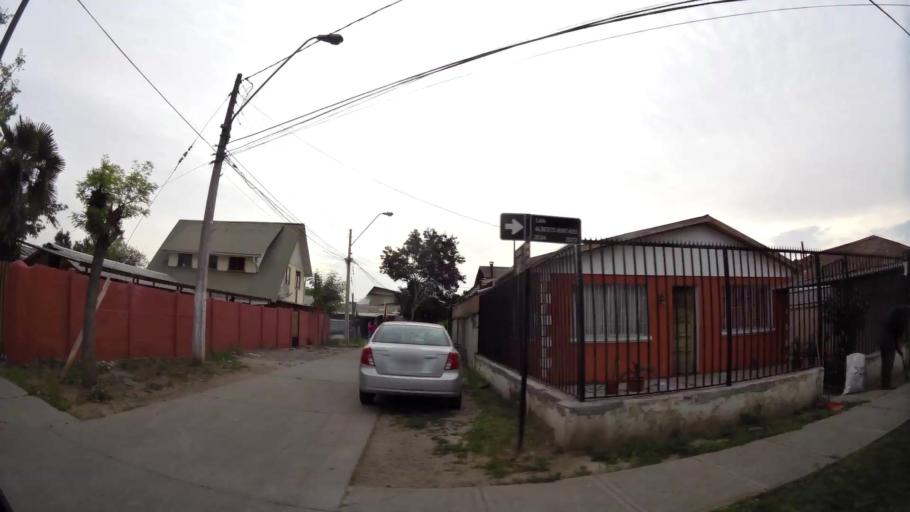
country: CL
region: Santiago Metropolitan
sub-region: Provincia de Santiago
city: Lo Prado
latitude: -33.5111
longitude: -70.7691
